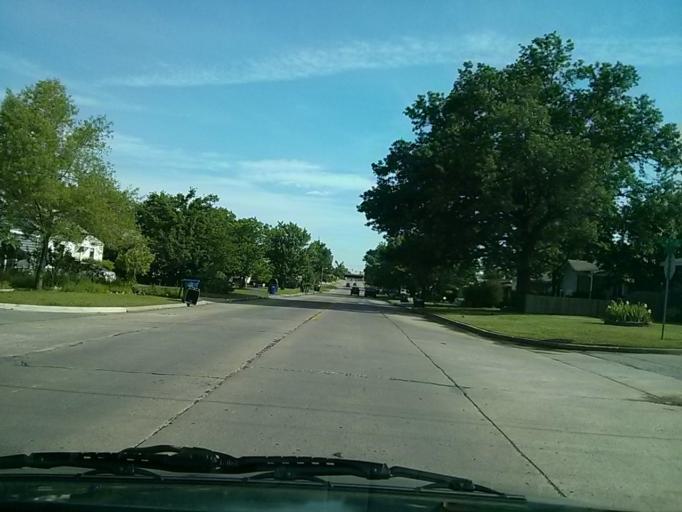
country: US
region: Oklahoma
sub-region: Tulsa County
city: Tulsa
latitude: 36.1571
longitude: -95.8956
